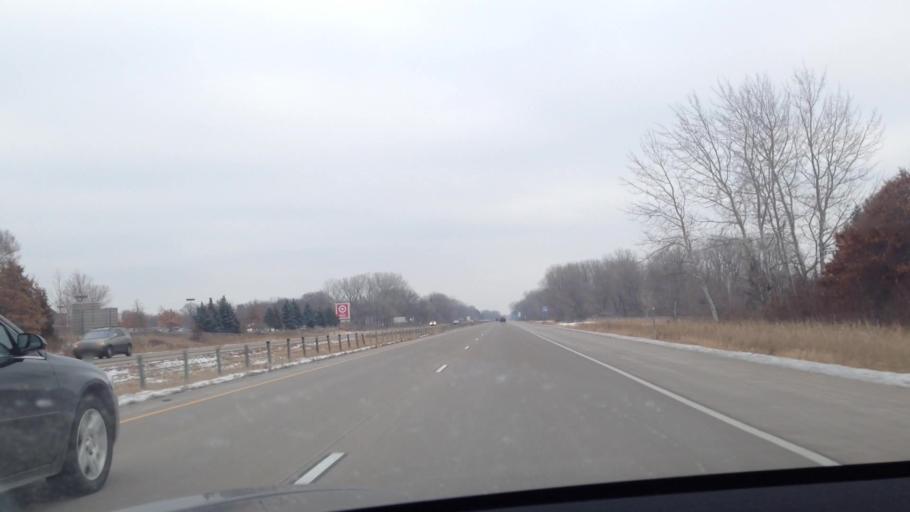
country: US
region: Minnesota
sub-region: Anoka County
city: Lino Lakes
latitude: 45.1818
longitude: -93.1077
